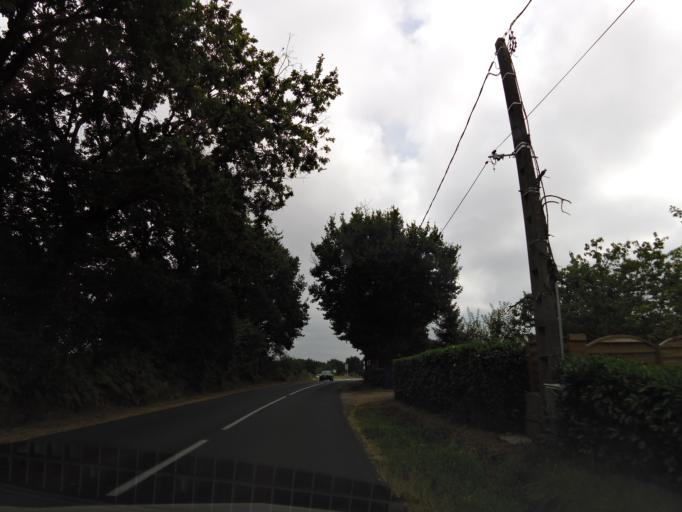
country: FR
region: Pays de la Loire
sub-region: Departement de la Vendee
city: Avrille
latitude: 46.4610
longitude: -1.4560
